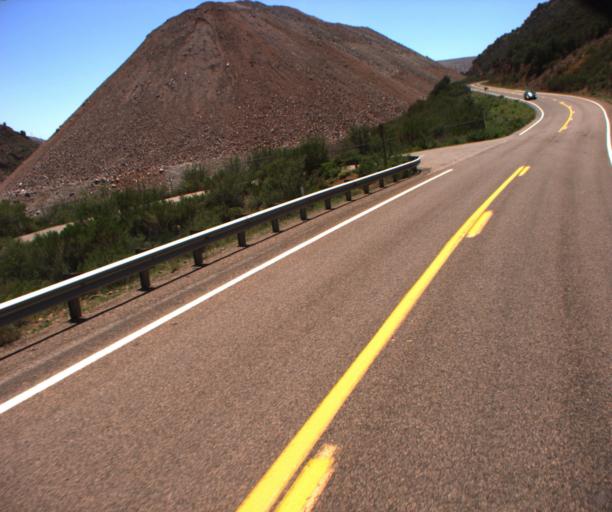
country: US
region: Arizona
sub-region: Greenlee County
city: Morenci
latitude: 33.1455
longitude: -109.3745
